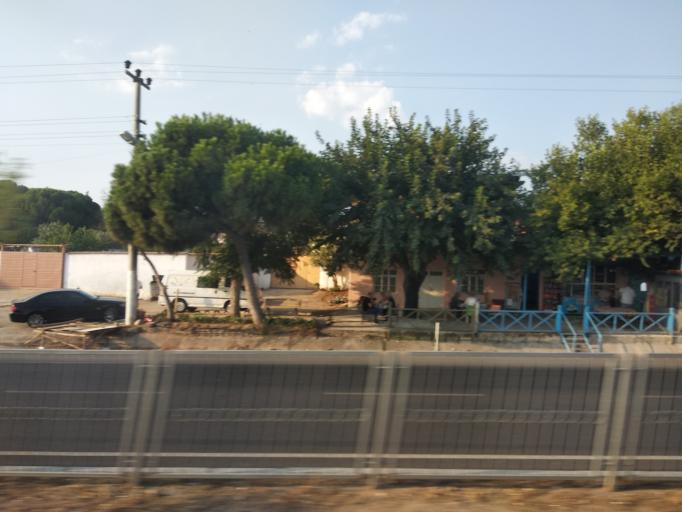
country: TR
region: Manisa
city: Ahmetli
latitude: 38.5057
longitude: 28.0007
